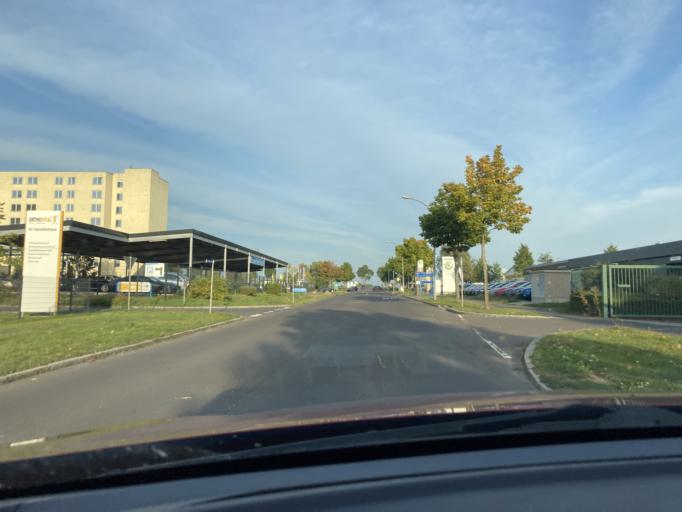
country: DE
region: Saxony
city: Markkleeberg
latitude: 51.2808
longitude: 12.4268
